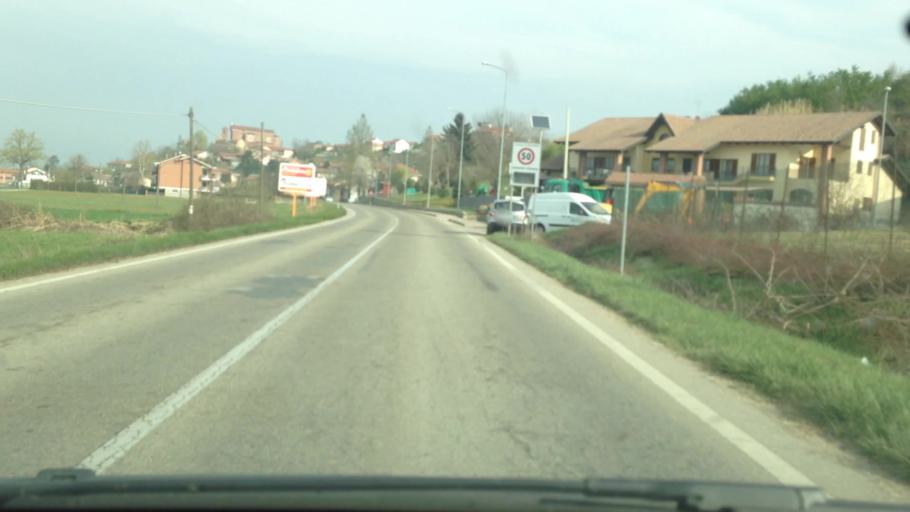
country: IT
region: Piedmont
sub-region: Provincia di Torino
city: Pralormo
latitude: 44.8544
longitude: 7.9075
